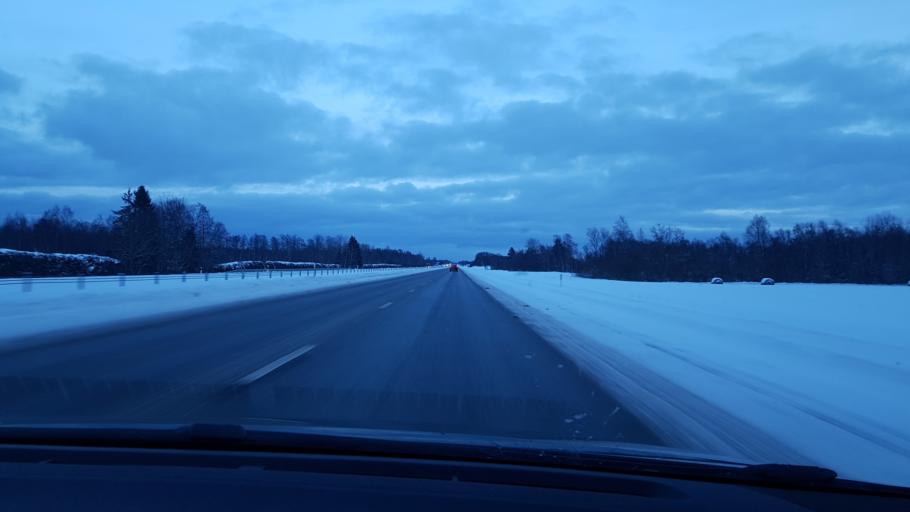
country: EE
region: Harju
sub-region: Anija vald
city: Kehra
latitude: 59.4424
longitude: 25.3278
